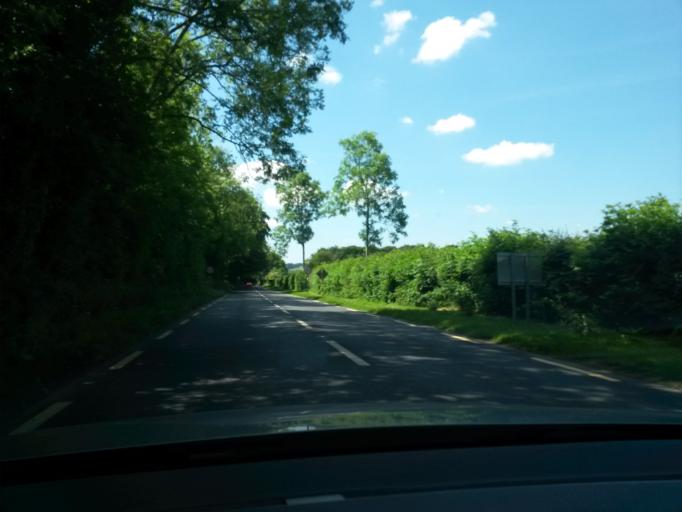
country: IE
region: Leinster
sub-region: Wicklow
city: Blessington
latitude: 53.1631
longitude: -6.5448
